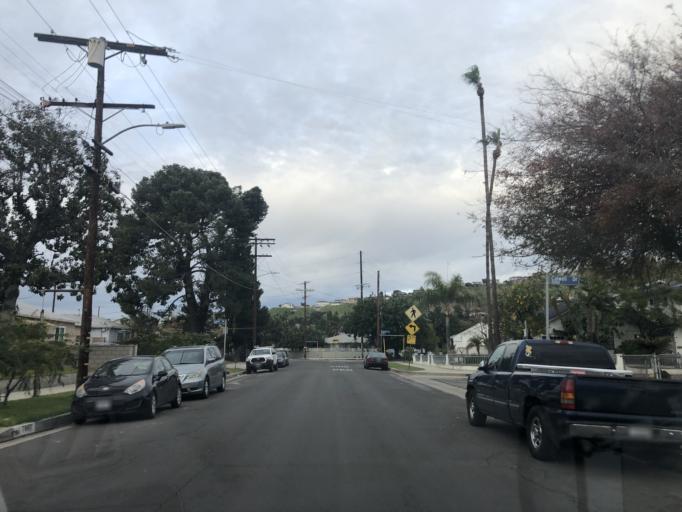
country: US
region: California
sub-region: Los Angeles County
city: North Hollywood
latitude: 34.2134
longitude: -118.3535
